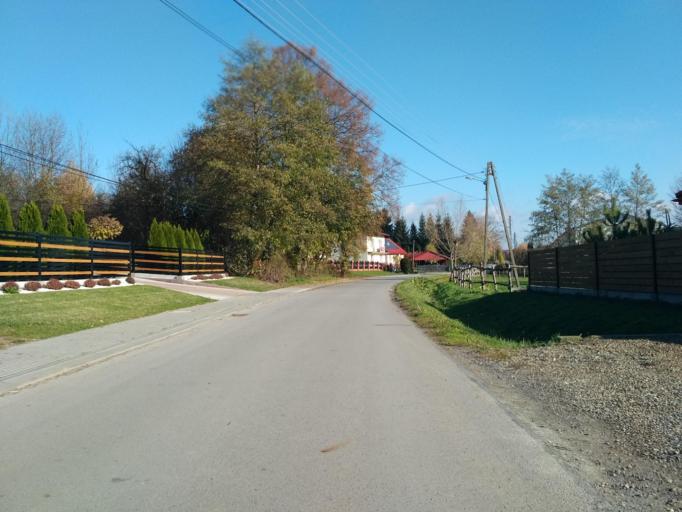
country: PL
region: Subcarpathian Voivodeship
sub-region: Powiat rzeszowski
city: Niechobrz
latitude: 49.9922
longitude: 21.8680
